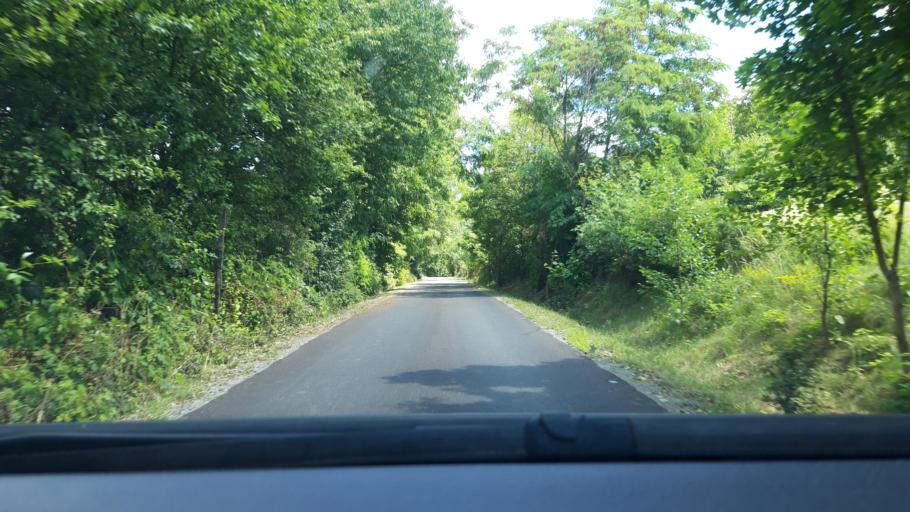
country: HU
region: Nograd
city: Somoskoujfalu
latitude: 48.1833
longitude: 19.8450
